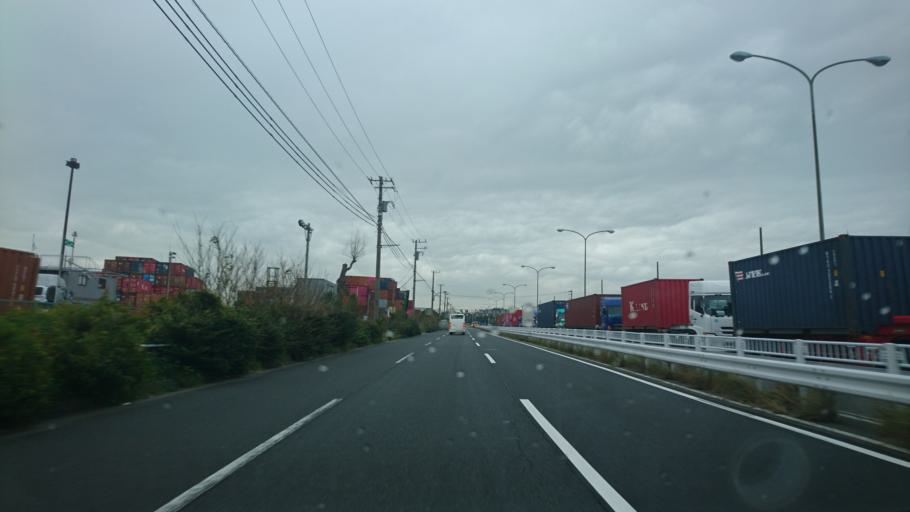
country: JP
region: Kanagawa
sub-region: Kawasaki-shi
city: Kawasaki
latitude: 35.6037
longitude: 139.7610
